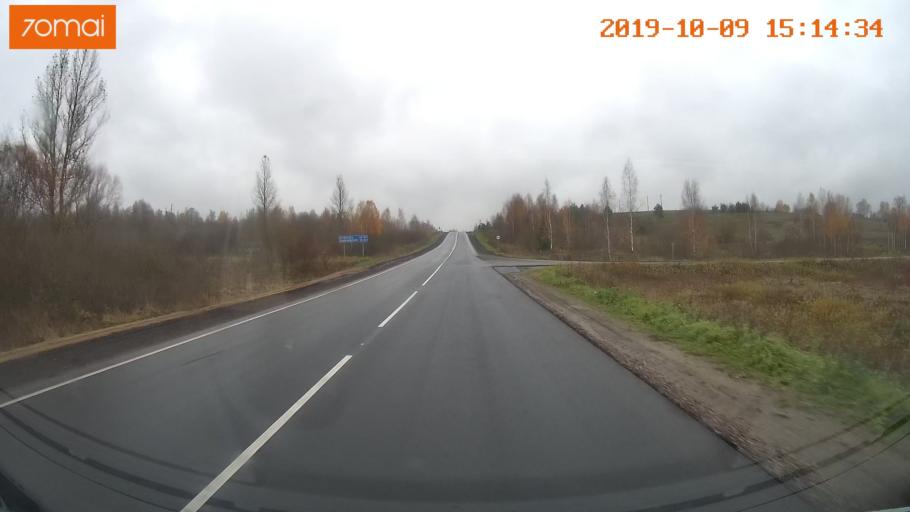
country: RU
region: Kostroma
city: Susanino
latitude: 58.1327
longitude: 41.6019
